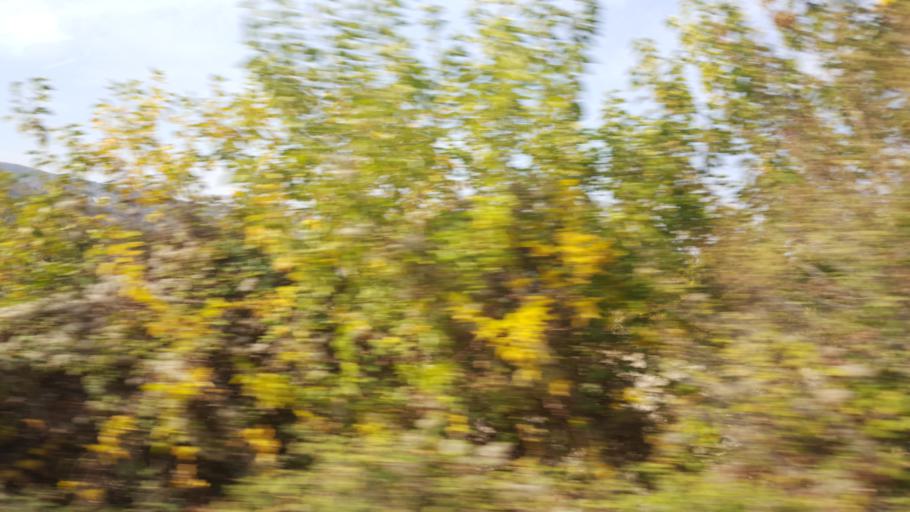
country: TR
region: Eskisehir
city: Mihaliccik
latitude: 39.9788
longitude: 31.3752
